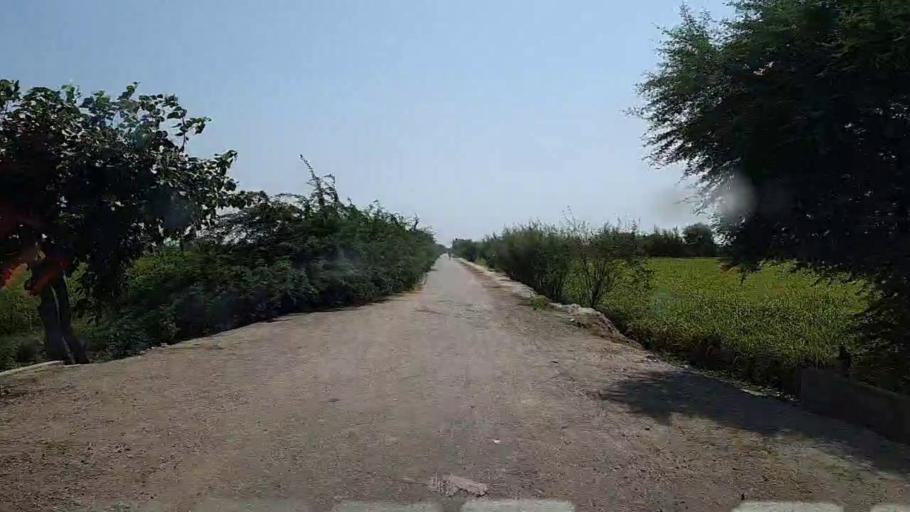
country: PK
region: Sindh
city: Mirpur Batoro
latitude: 24.6170
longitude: 68.4522
